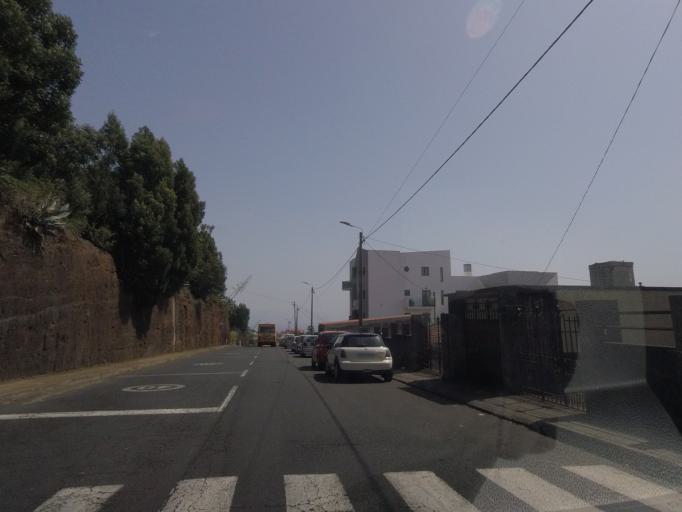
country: PT
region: Madeira
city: Camara de Lobos
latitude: 32.6620
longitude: -16.9471
